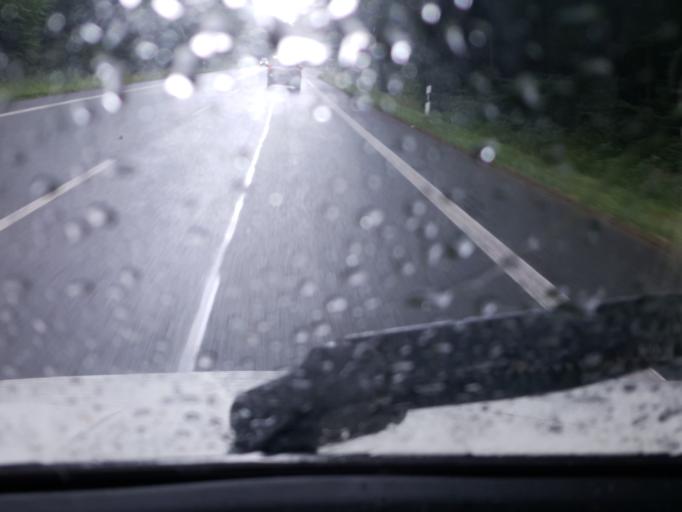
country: DE
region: North Rhine-Westphalia
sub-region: Regierungsbezirk Detmold
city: Petershagen
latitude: 52.3501
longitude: 8.9489
